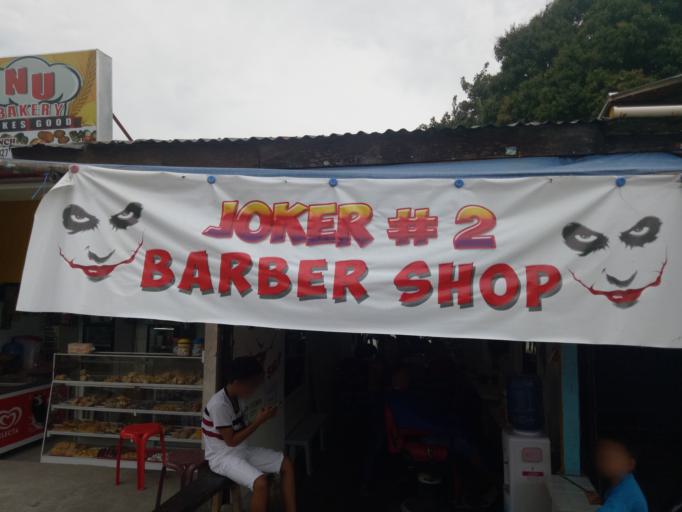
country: PH
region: Central Visayas
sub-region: Province of Negros Oriental
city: Dumaguete
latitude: 9.3045
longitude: 123.3029
